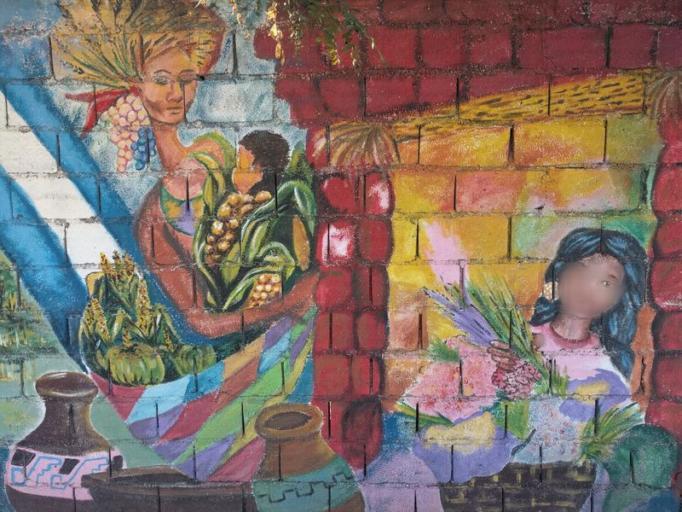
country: AR
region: Salta
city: Salta
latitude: -24.8123
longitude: -65.4179
